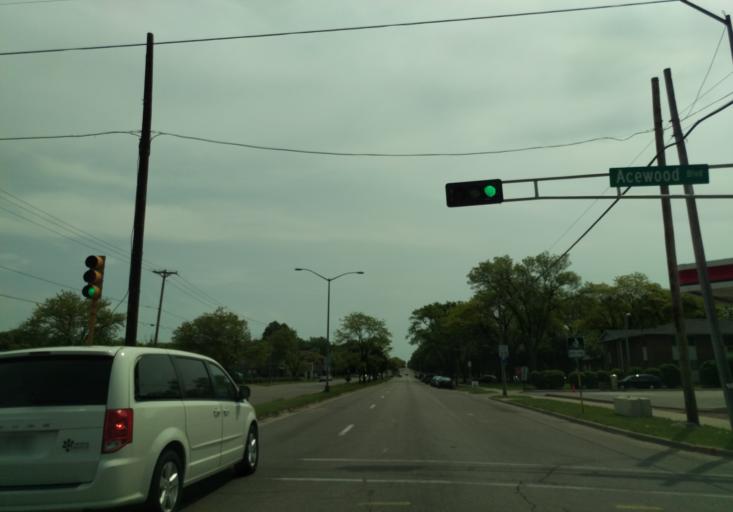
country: US
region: Wisconsin
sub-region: Dane County
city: Monona
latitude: 43.0842
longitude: -89.3029
